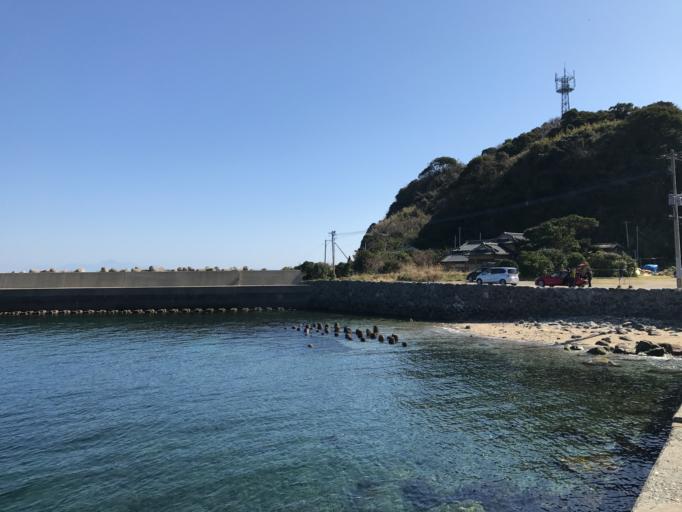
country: JP
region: Nagasaki
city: Nagasaki-shi
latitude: 32.5689
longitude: 129.7858
